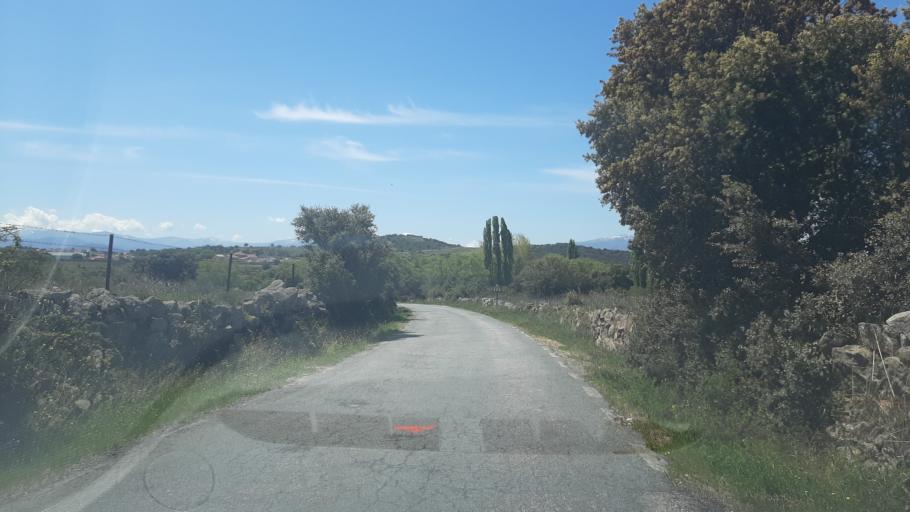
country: ES
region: Castille and Leon
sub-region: Provincia de Avila
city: Narrillos del Alamo
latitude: 40.5461
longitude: -5.4471
